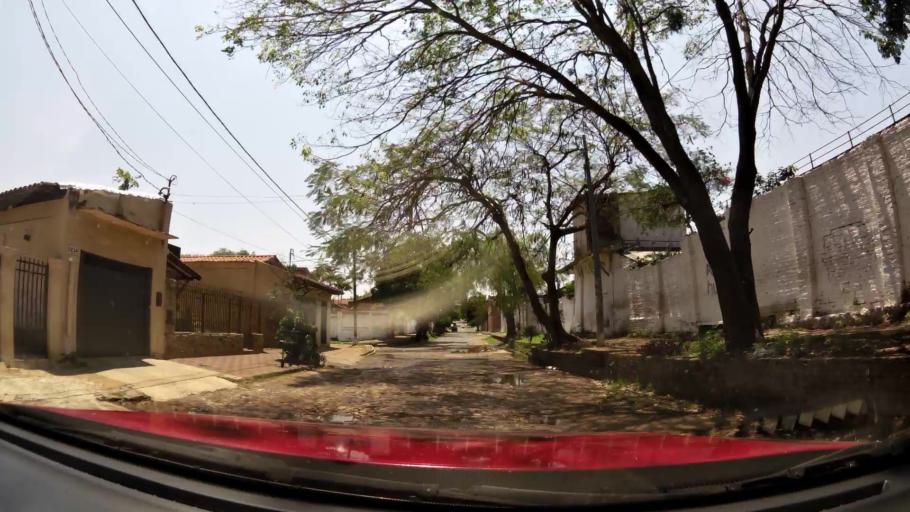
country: PY
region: Asuncion
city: Asuncion
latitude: -25.2960
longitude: -57.6483
